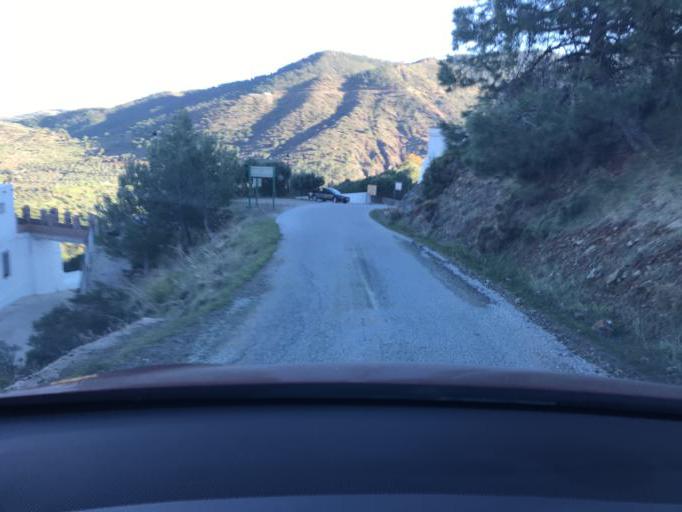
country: ES
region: Andalusia
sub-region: Provincia de Malaga
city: Tolox
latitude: 36.6850
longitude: -4.9114
